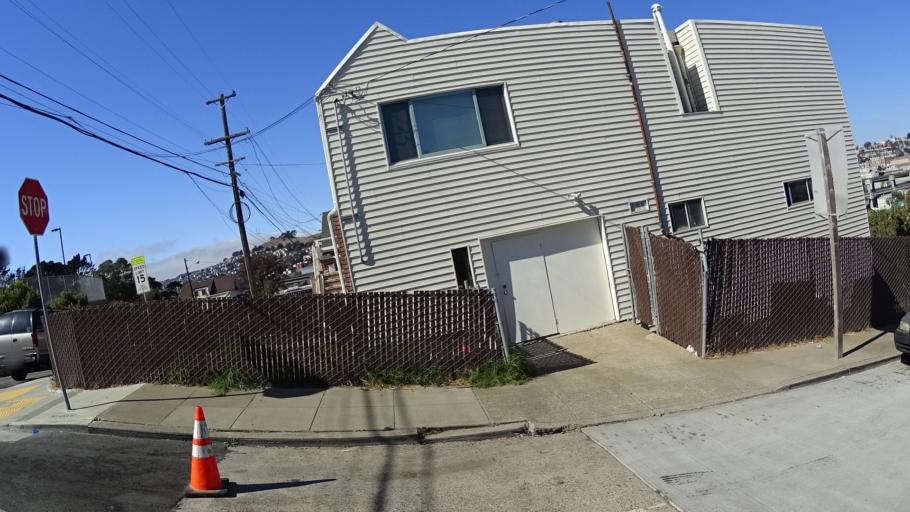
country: US
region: California
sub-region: San Francisco County
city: San Francisco
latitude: 37.7371
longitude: -122.3994
